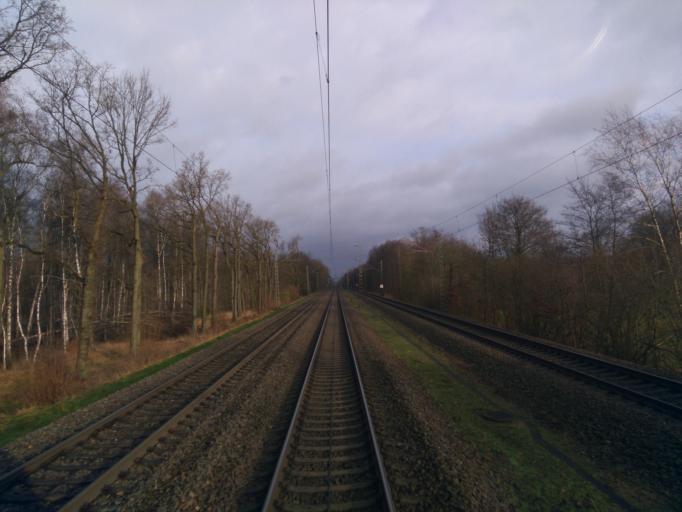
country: DE
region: Lower Saxony
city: Wistedt
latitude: 53.2577
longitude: 9.7009
